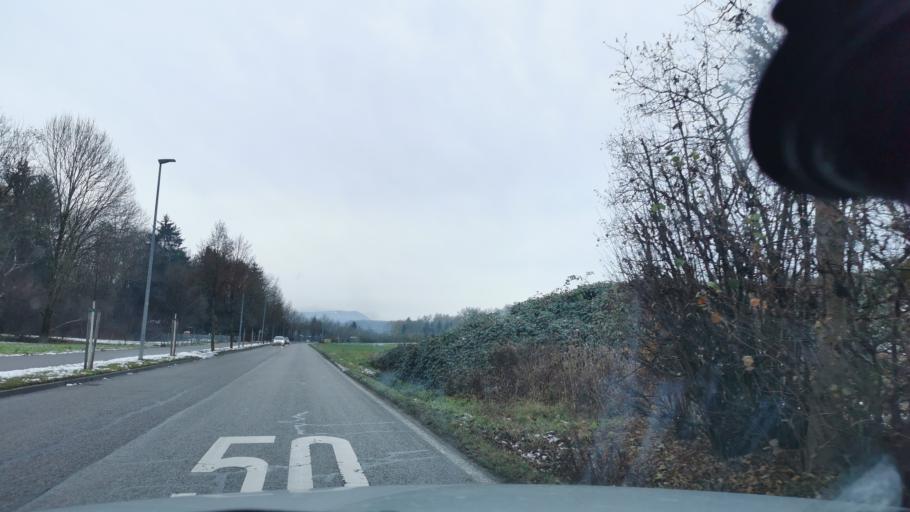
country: DE
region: Baden-Wuerttemberg
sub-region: Regierungsbezirk Stuttgart
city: Eislingen
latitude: 48.7109
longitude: 9.6830
